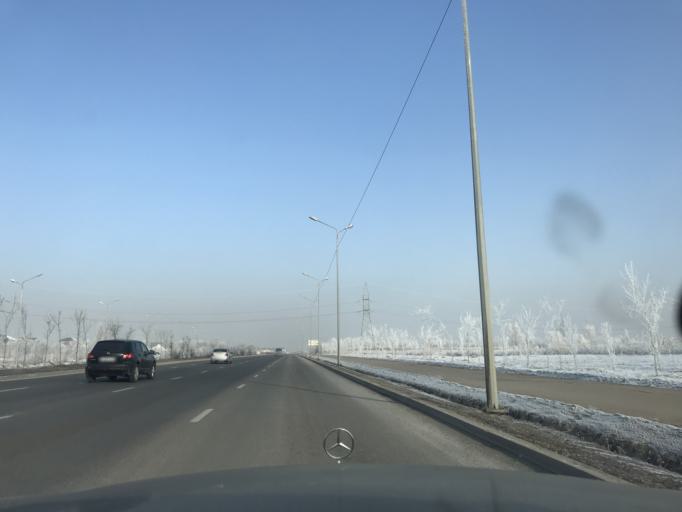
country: KZ
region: Almaty Oblysy
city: Burunday
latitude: 43.3320
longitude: 76.8335
